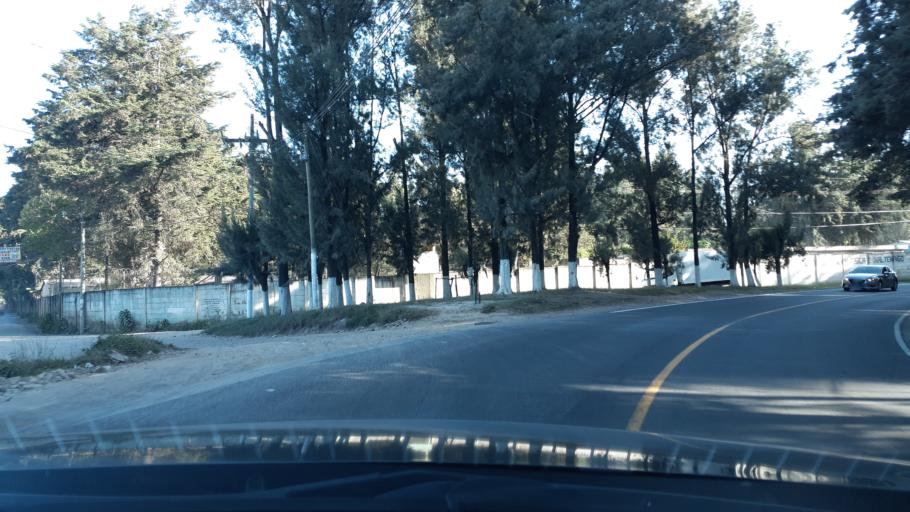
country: GT
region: Chimaltenango
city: El Tejar
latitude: 14.6413
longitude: -90.8090
